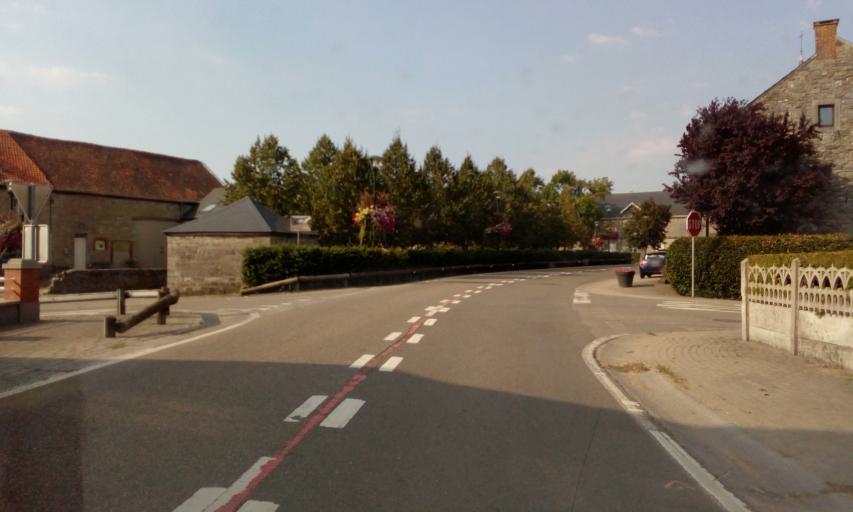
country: BE
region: Wallonia
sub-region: Province de Namur
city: Rochefort
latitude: 50.1204
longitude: 5.2480
